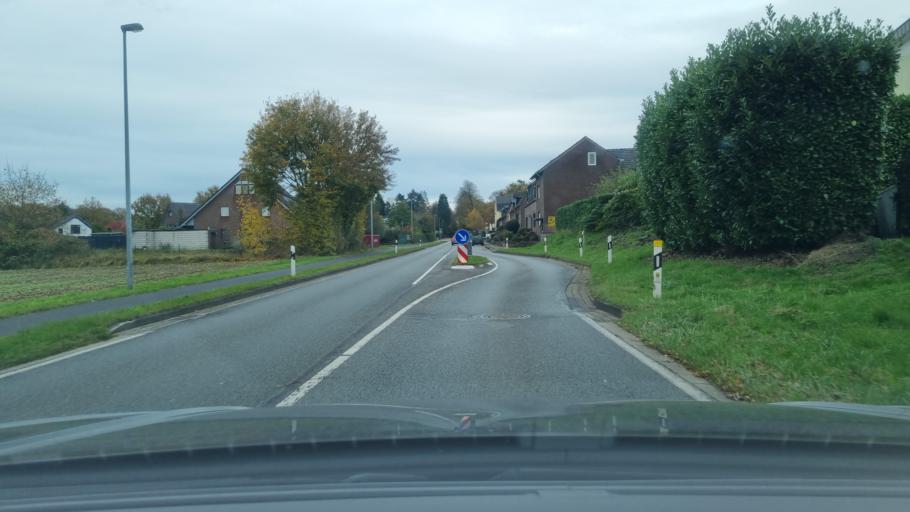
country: DE
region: North Rhine-Westphalia
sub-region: Regierungsbezirk Dusseldorf
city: Kleve
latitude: 51.7907
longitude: 6.1104
